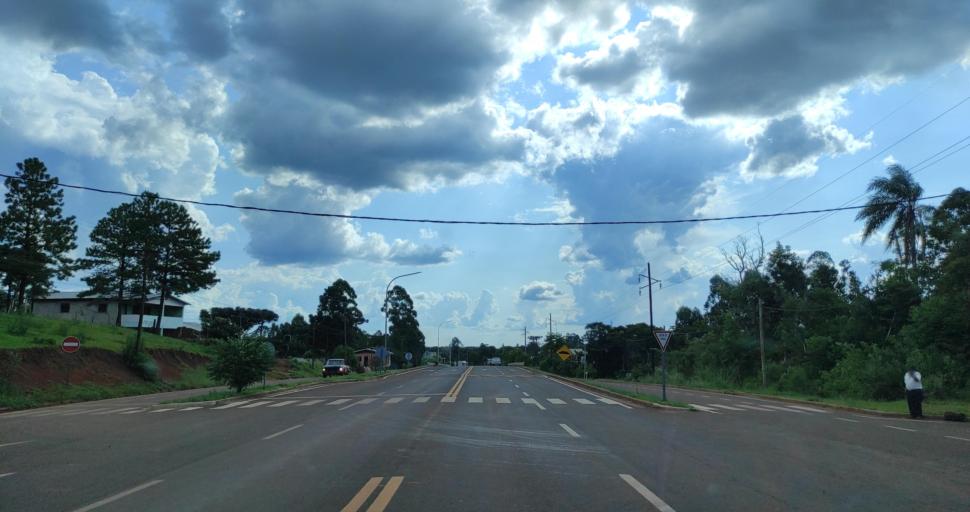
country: AR
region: Misiones
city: Bernardo de Irigoyen
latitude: -26.2943
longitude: -53.7453
